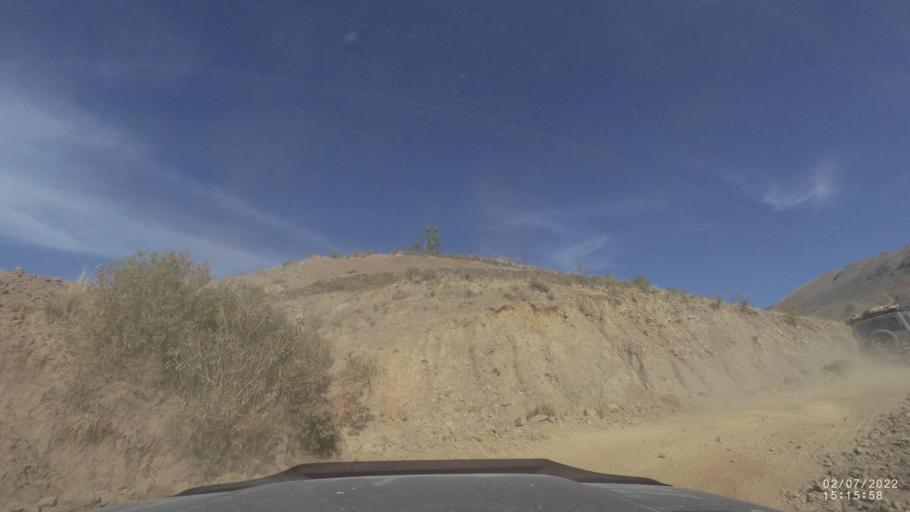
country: BO
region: Cochabamba
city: Irpa Irpa
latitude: -17.8638
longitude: -66.4331
